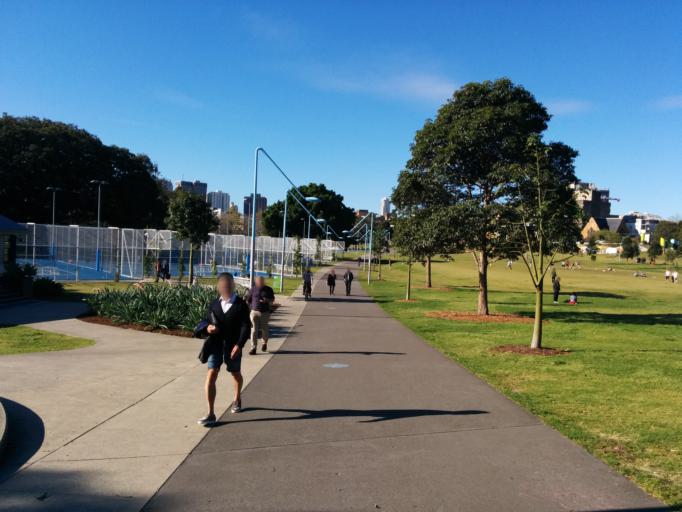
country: AU
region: New South Wales
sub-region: City of Sydney
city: Redfern
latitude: -33.8887
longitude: 151.2035
